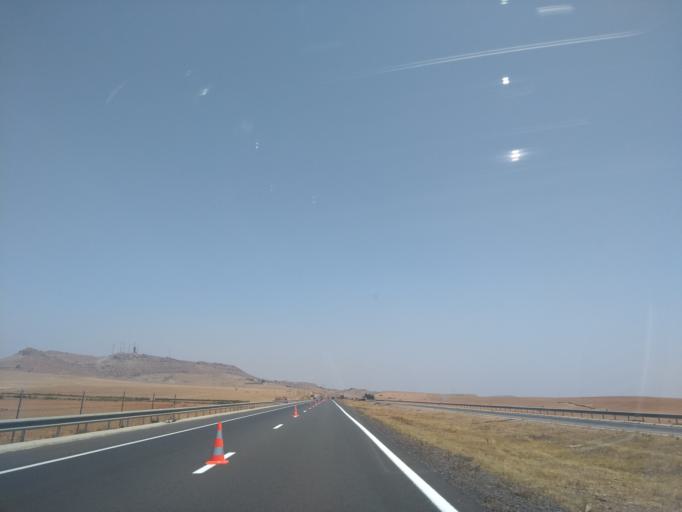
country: MA
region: Marrakech-Tensift-Al Haouz
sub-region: Kelaa-Des-Sraghna
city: Sidi Abdallah
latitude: 32.4518
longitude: -7.9314
